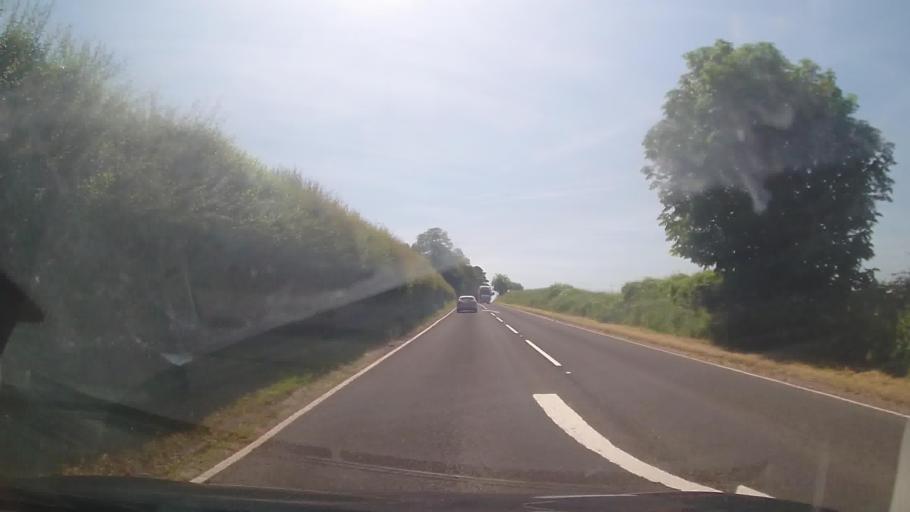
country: GB
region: England
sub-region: Herefordshire
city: Hereford
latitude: 52.0906
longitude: -2.7255
